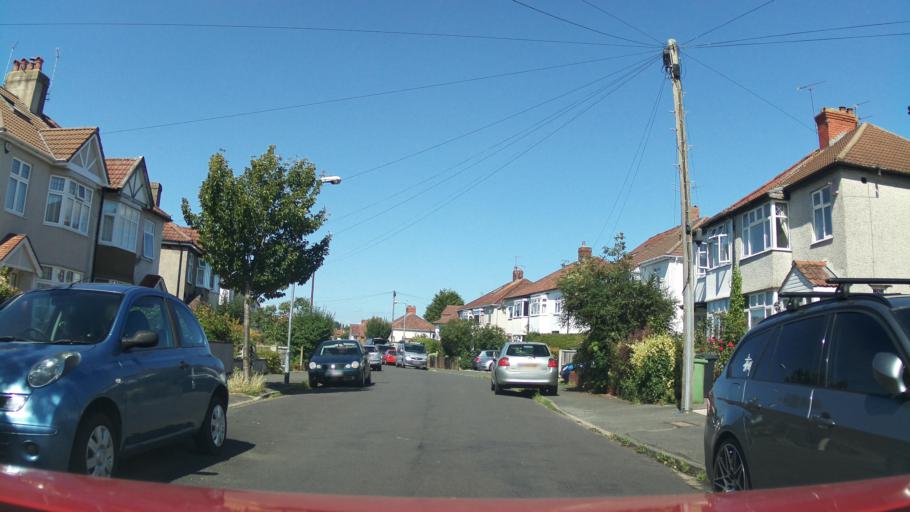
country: GB
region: England
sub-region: Bristol
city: Bristol
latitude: 51.4965
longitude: -2.6029
